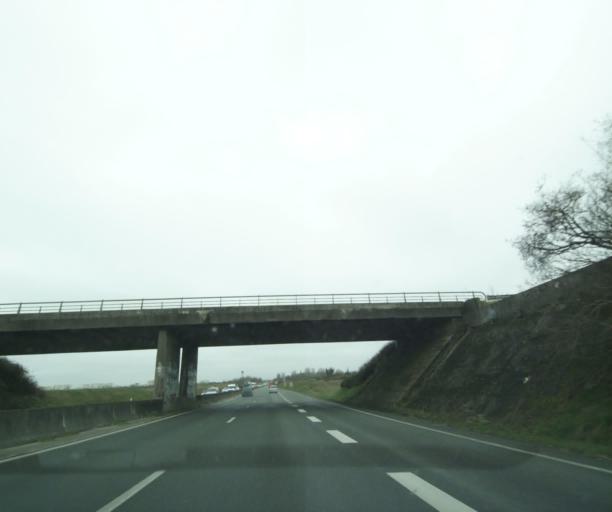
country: FR
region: Poitou-Charentes
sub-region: Departement de la Charente-Maritime
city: Aytre
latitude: 46.1424
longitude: -1.1068
